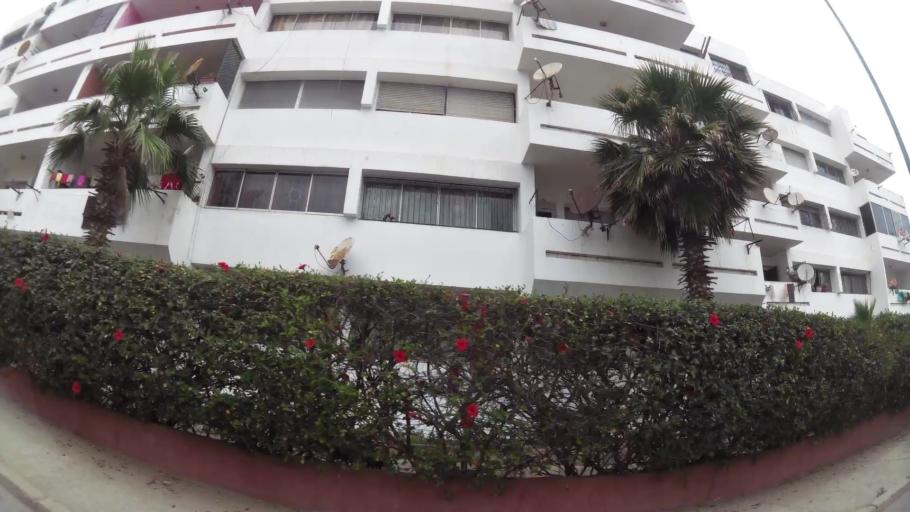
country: MA
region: Rabat-Sale-Zemmour-Zaer
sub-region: Rabat
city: Rabat
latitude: 33.9926
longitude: -6.8796
